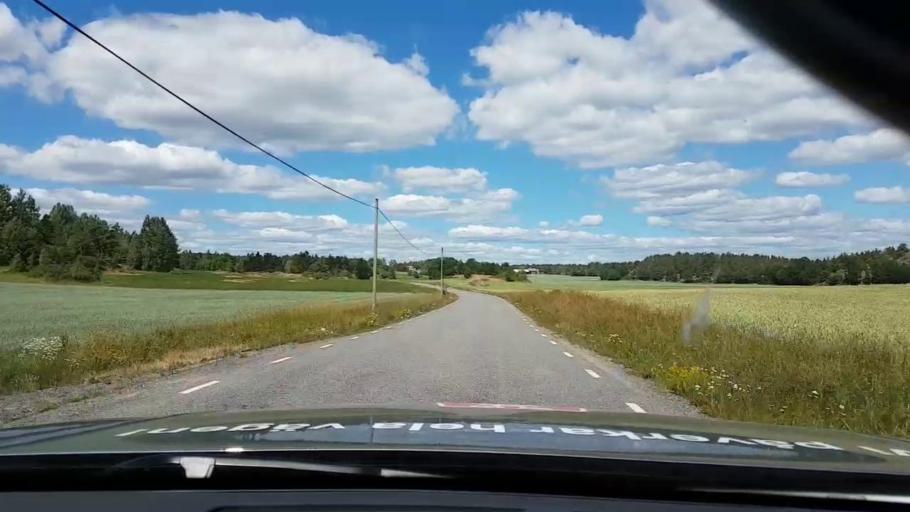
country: SE
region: Kalmar
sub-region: Vasterviks Kommun
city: Forserum
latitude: 58.0018
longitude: 16.5902
